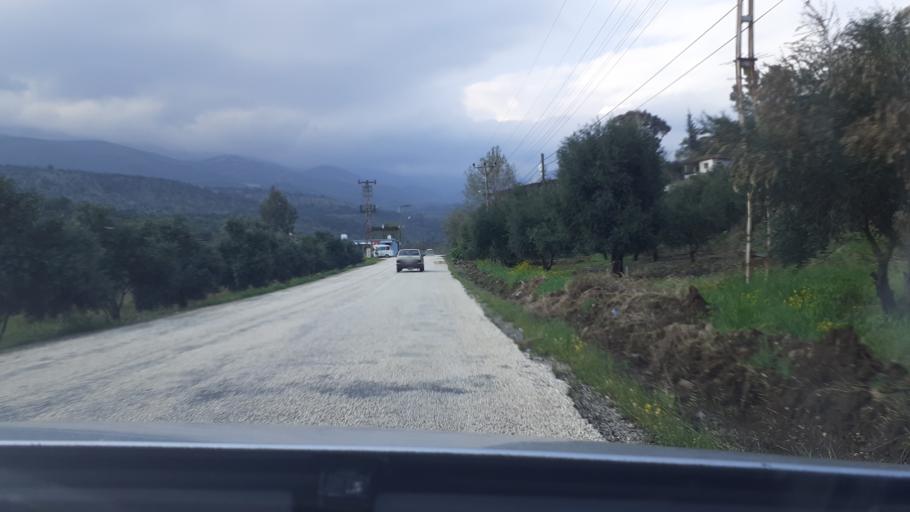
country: TR
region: Hatay
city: Kirikhan
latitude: 36.5050
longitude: 36.3233
